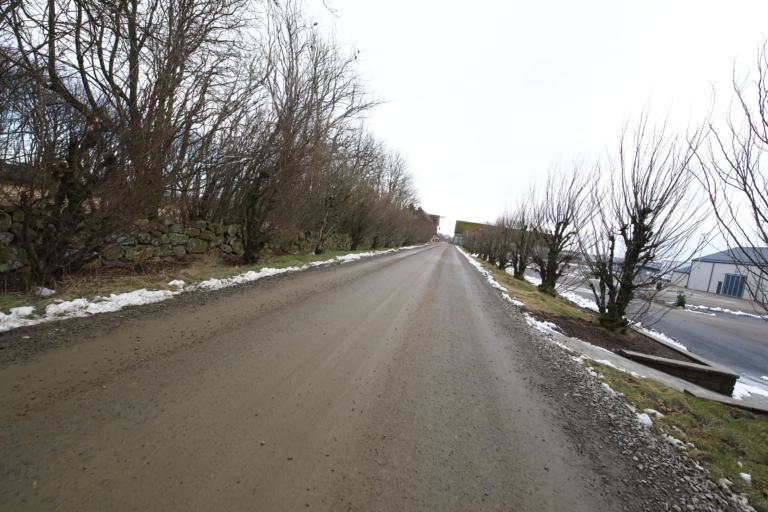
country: SE
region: Halland
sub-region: Varbergs Kommun
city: Varberg
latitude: 57.1242
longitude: 12.3009
